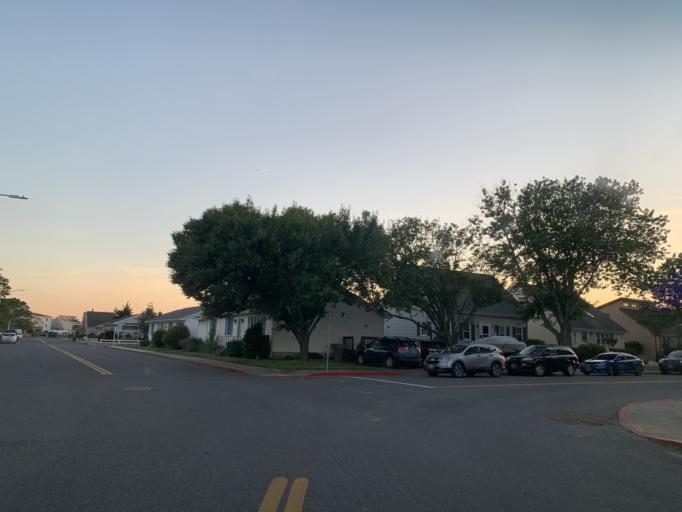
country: US
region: Delaware
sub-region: Sussex County
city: Bethany Beach
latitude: 38.4495
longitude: -75.0614
